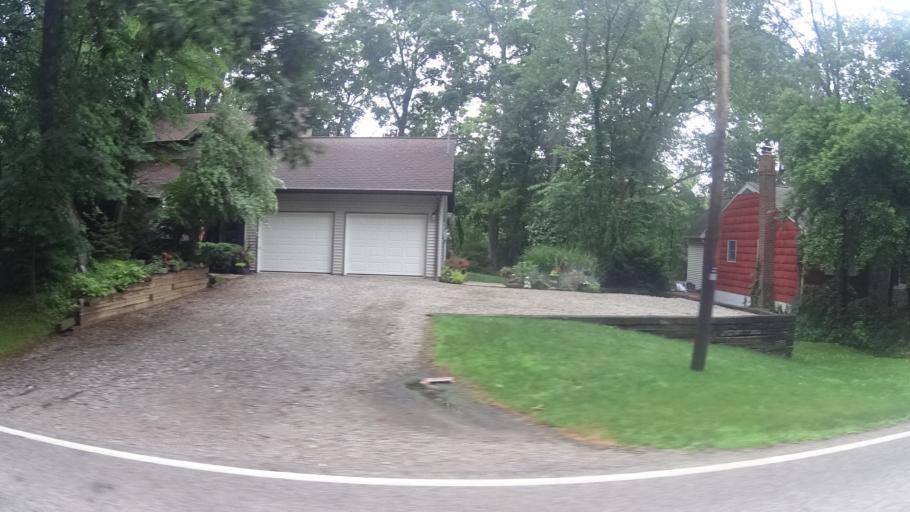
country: US
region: Ohio
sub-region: Erie County
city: Huron
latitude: 41.3582
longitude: -82.5837
